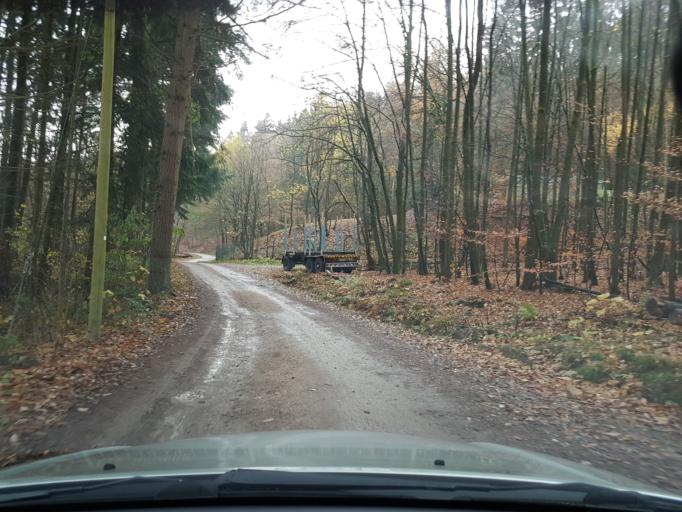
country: DE
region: Hesse
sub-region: Regierungsbezirk Darmstadt
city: Kiedrich
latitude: 50.0492
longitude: 8.0425
